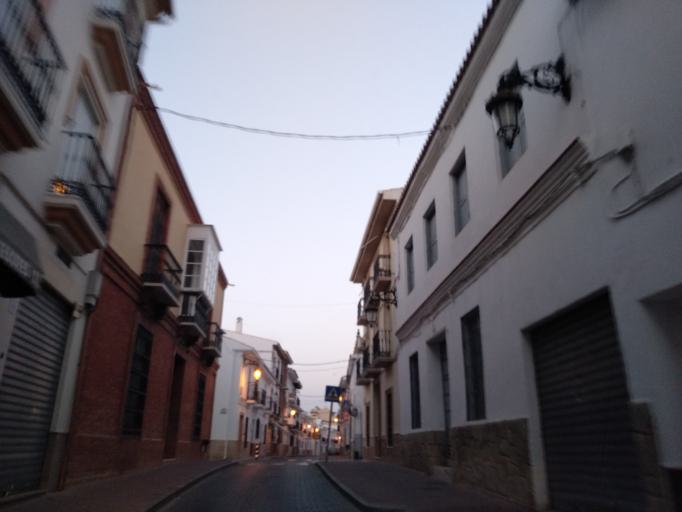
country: ES
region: Andalusia
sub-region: Provincia de Malaga
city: Cartama
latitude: 36.7113
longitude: -4.6309
